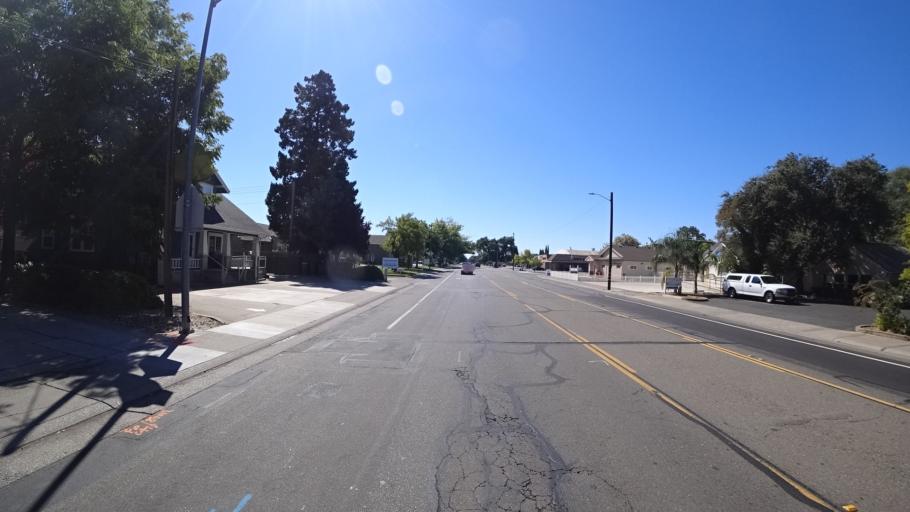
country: US
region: California
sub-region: Sacramento County
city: Elk Grove
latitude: 38.4080
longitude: -121.3714
